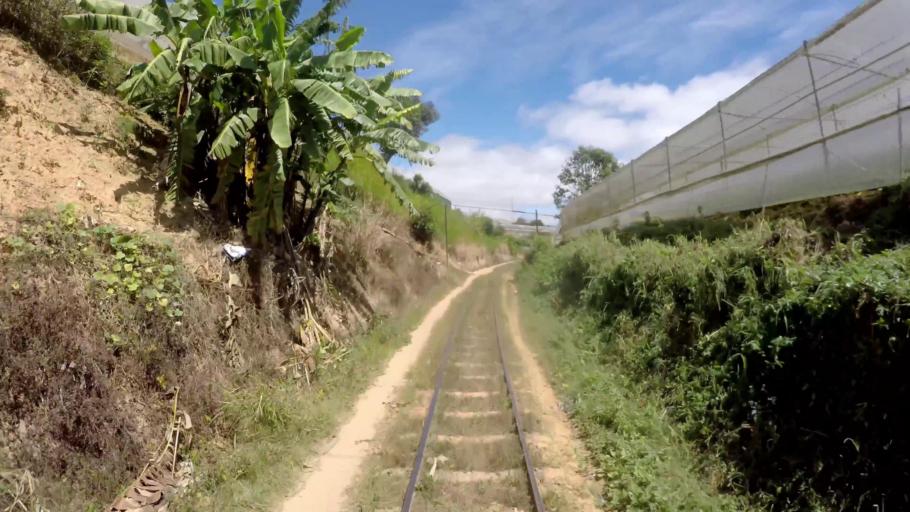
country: VN
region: Lam Dong
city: Da Lat
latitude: 11.9511
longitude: 108.4729
